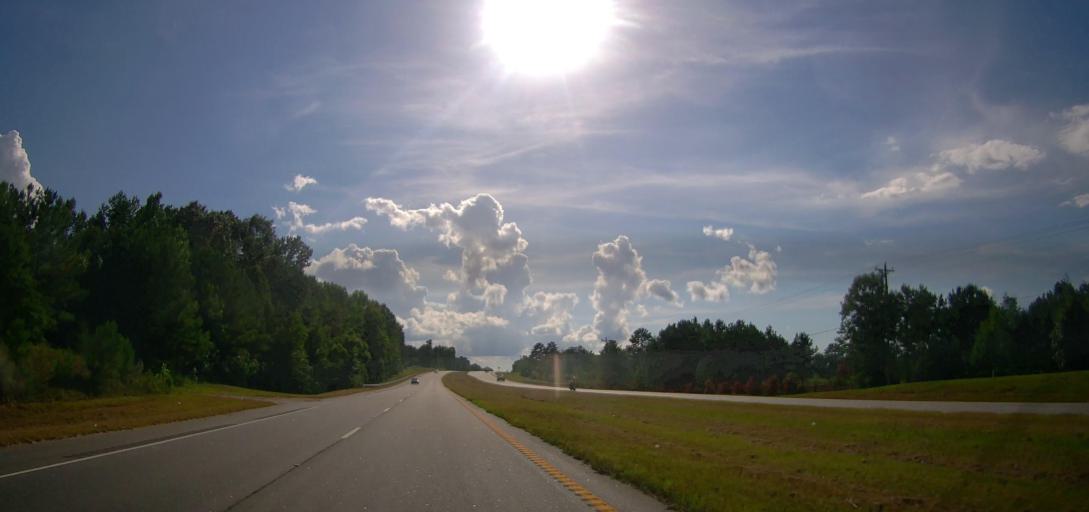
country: US
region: Georgia
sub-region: Talbot County
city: Talbotton
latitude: 32.5754
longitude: -84.5726
